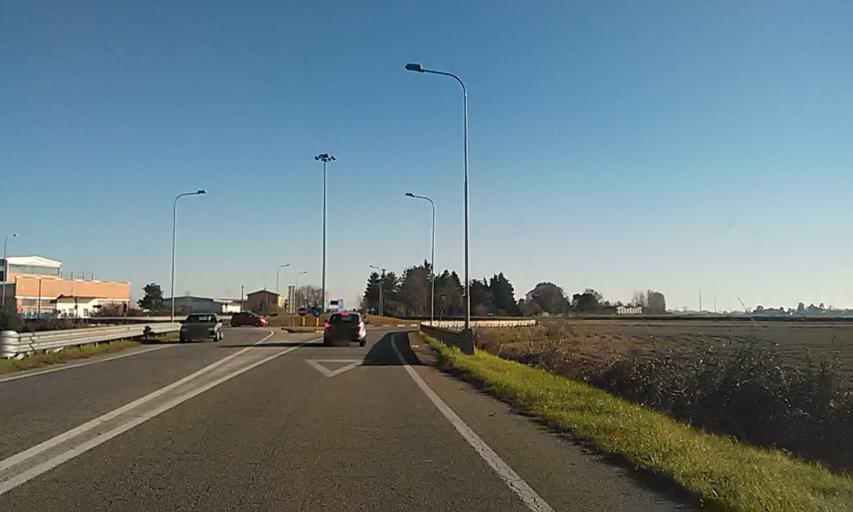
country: IT
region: Piedmont
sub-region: Provincia di Vercelli
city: Prarolo
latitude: 45.2902
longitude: 8.4531
